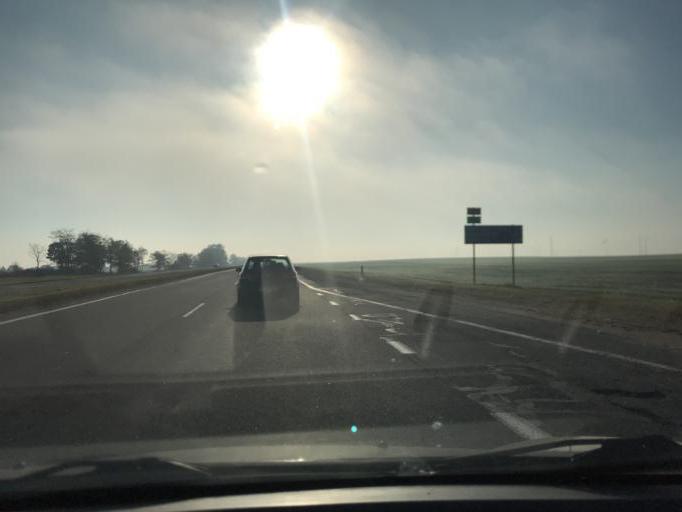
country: BY
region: Minsk
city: Dukora
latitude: 53.7023
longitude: 27.8818
